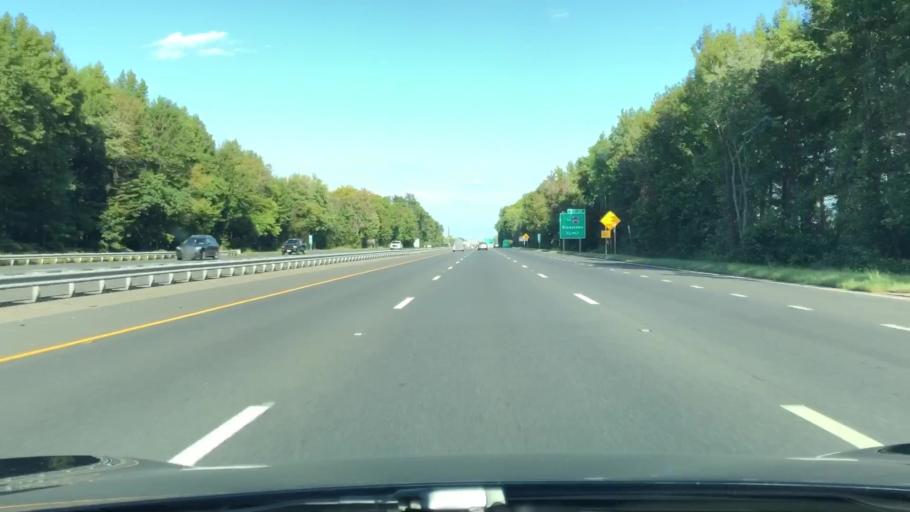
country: US
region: New Jersey
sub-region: Gloucester County
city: Gibbstown
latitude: 39.8121
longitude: -75.2707
